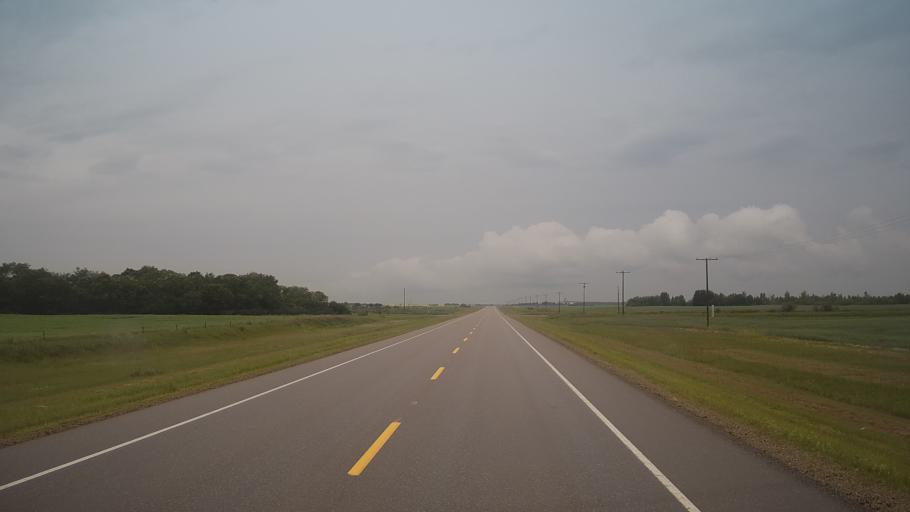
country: CA
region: Saskatchewan
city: Wilkie
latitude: 52.3167
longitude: -108.6983
